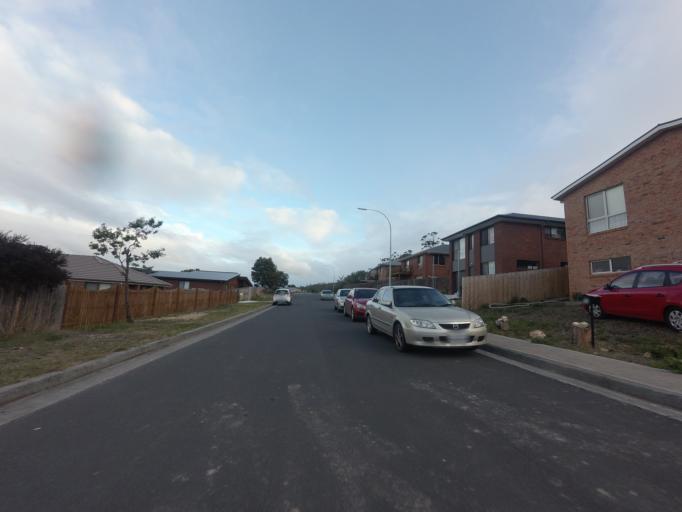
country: AU
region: Tasmania
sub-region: Clarence
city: Rokeby
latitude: -42.8984
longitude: 147.4287
